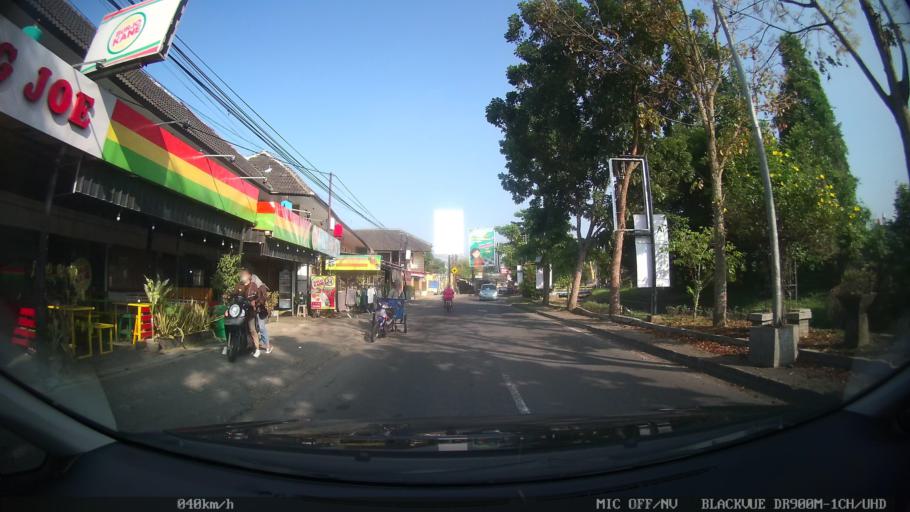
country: ID
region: Daerah Istimewa Yogyakarta
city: Depok
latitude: -7.7715
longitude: 110.4061
